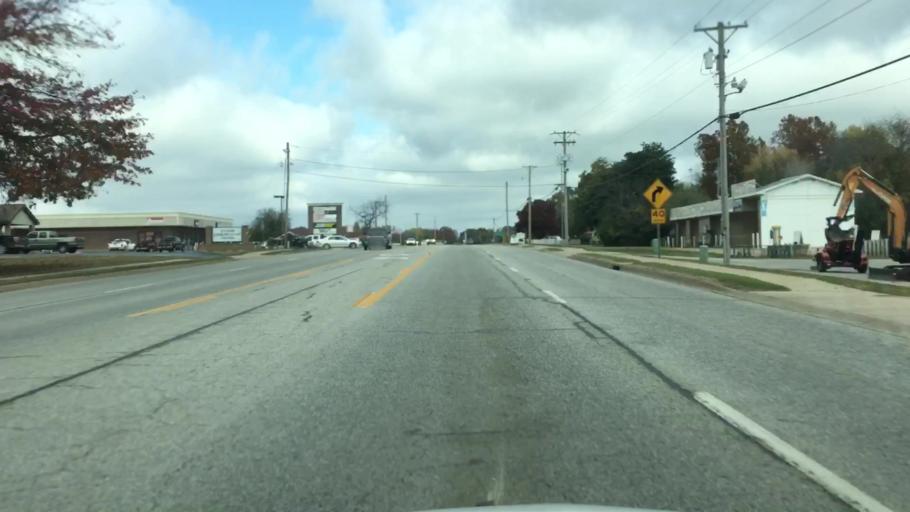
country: US
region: Arkansas
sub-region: Benton County
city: Gentry
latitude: 36.2563
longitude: -94.4852
